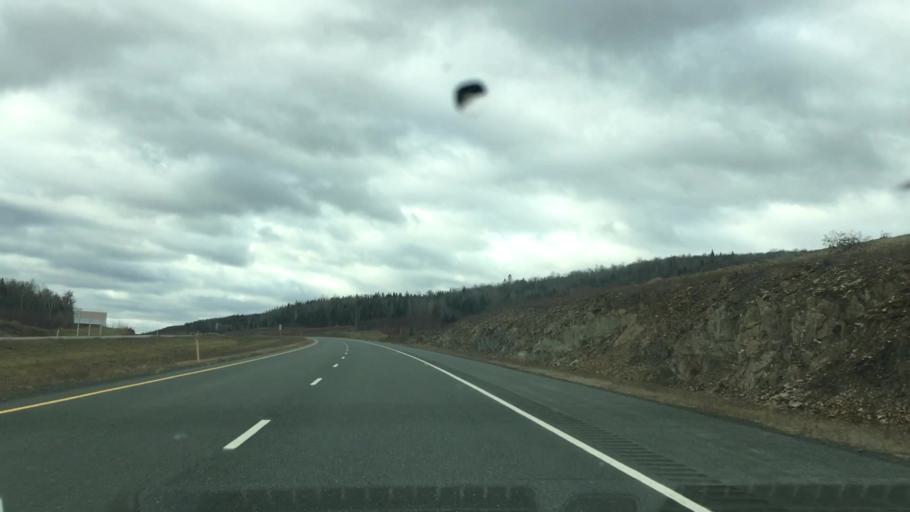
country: US
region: Maine
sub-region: Aroostook County
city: Fort Fairfield
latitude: 46.7289
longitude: -67.7255
